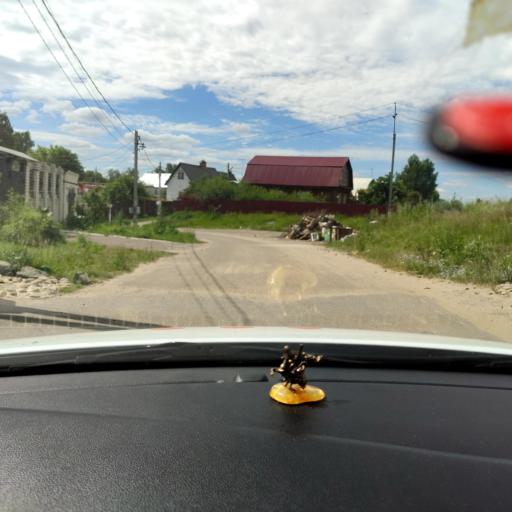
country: RU
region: Tatarstan
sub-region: Zelenodol'skiy Rayon
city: Vasil'yevo
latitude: 55.8355
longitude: 48.7184
